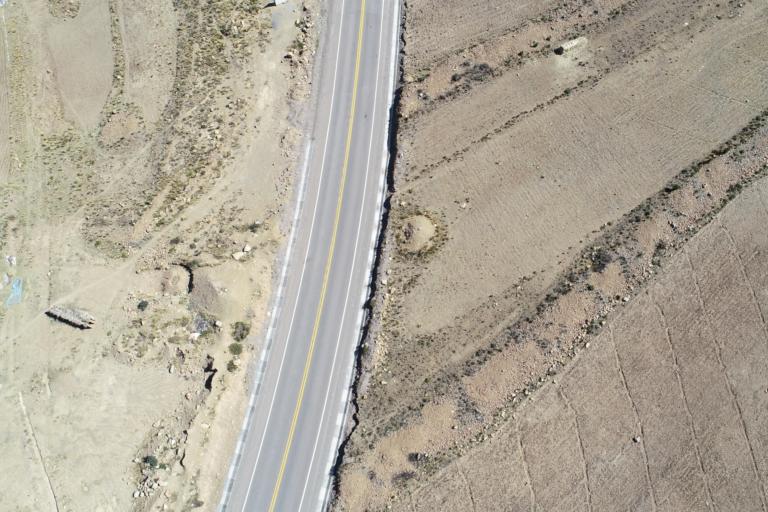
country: BO
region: La Paz
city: Achacachi
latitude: -15.8844
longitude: -68.8121
